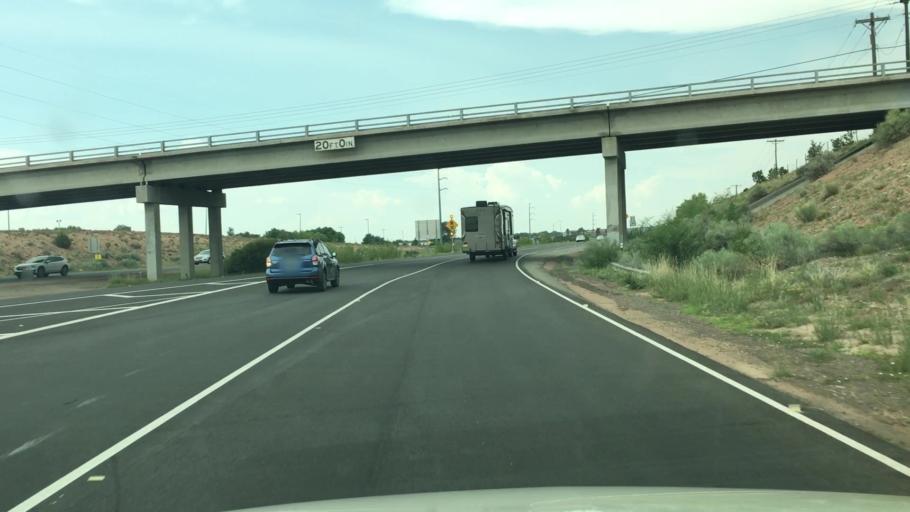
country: US
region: New Mexico
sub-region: Santa Fe County
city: Santa Fe
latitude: 35.6382
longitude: -105.9560
